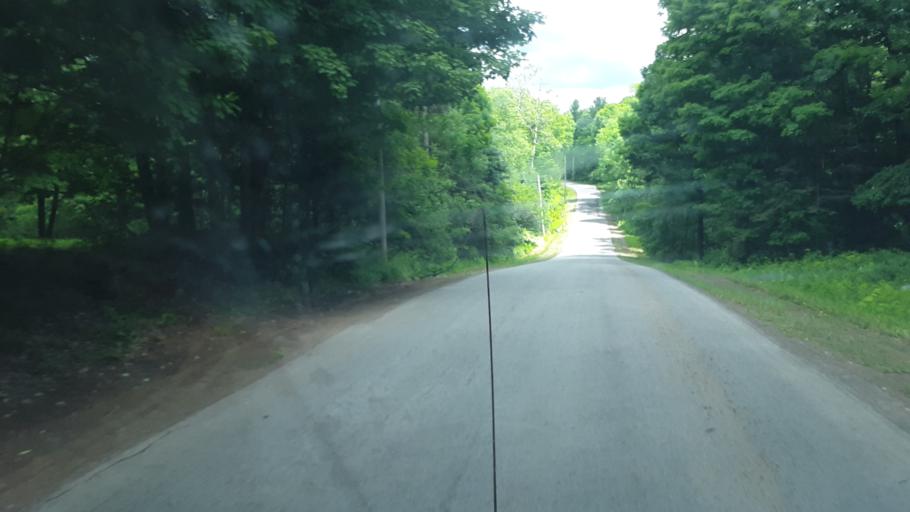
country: US
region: New York
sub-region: Oneida County
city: Rome
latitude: 43.3936
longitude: -75.5186
